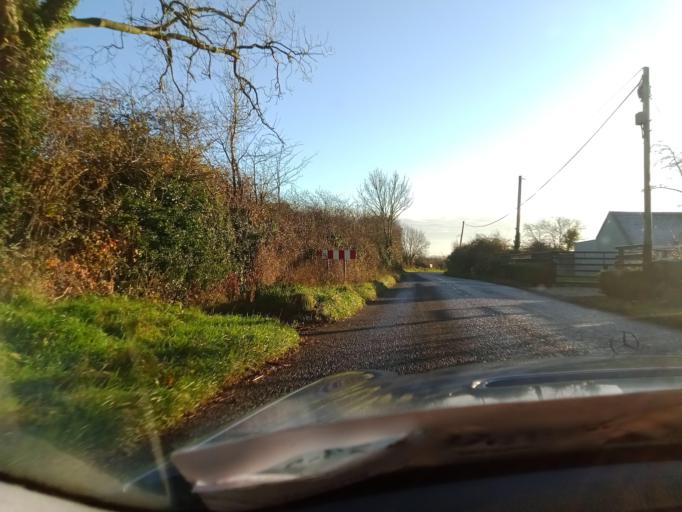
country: IE
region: Leinster
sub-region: Kilkenny
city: Callan
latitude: 52.5381
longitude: -7.3909
